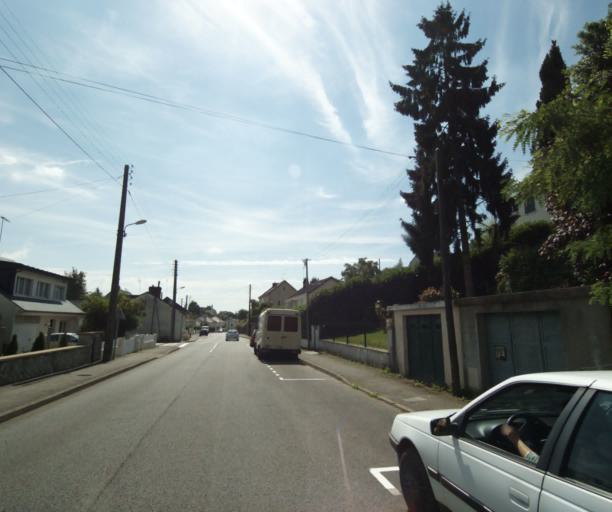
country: FR
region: Pays de la Loire
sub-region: Departement de la Mayenne
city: Laval
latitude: 48.0627
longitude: -0.7724
